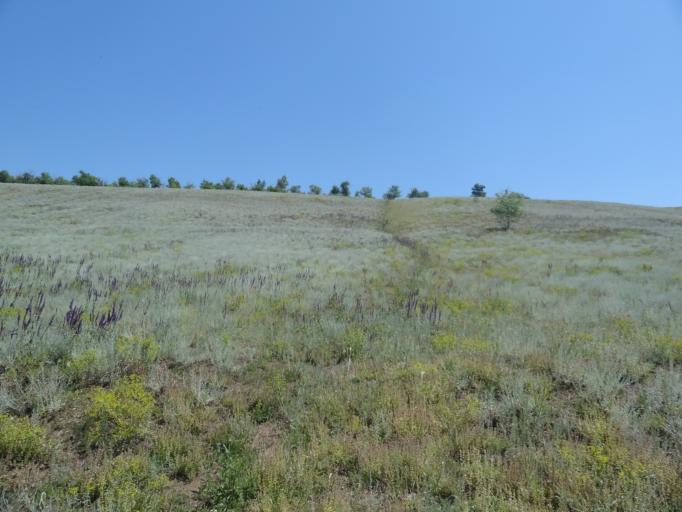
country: RU
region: Saratov
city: Krasnoarmeysk
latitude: 51.1113
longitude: 45.9387
